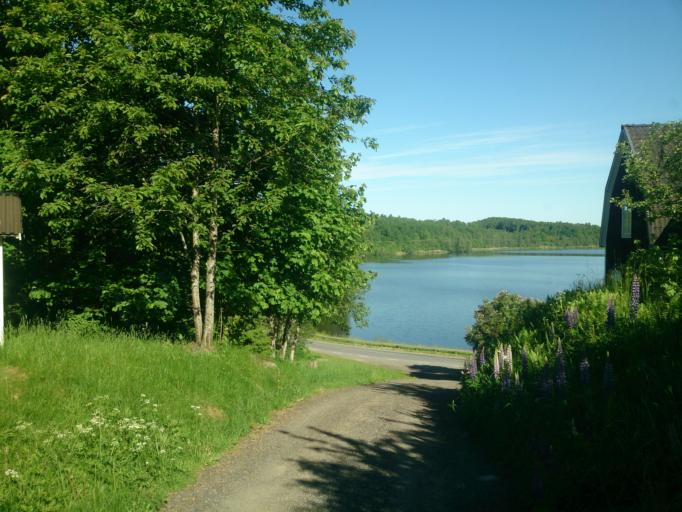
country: SE
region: OEstergoetland
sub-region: Atvidabergs Kommun
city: Atvidaberg
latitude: 58.1821
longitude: 16.0493
